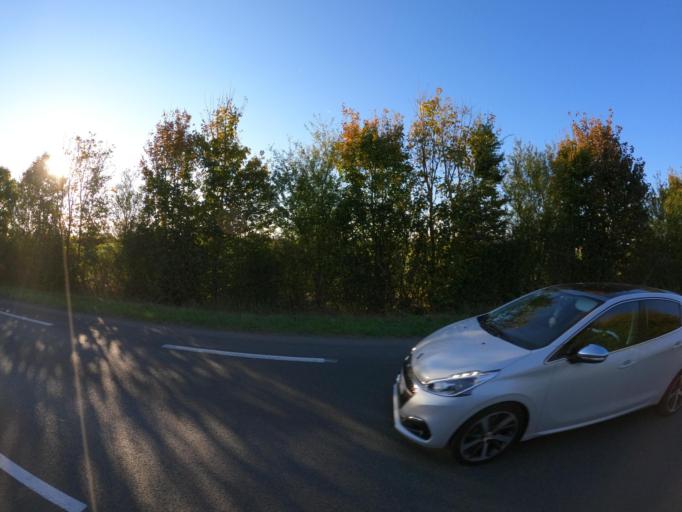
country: FR
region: Pays de la Loire
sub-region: Departement de la Vendee
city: Sainte-Gemme-la-Plaine
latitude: 46.5129
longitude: -1.0912
